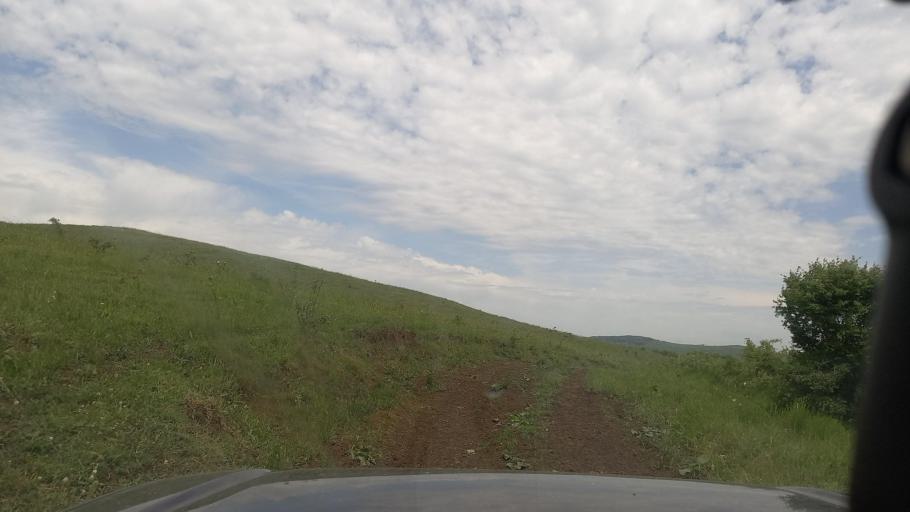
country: RU
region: Karachayevo-Cherkesiya
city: Pregradnaya
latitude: 44.0831
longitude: 41.2431
